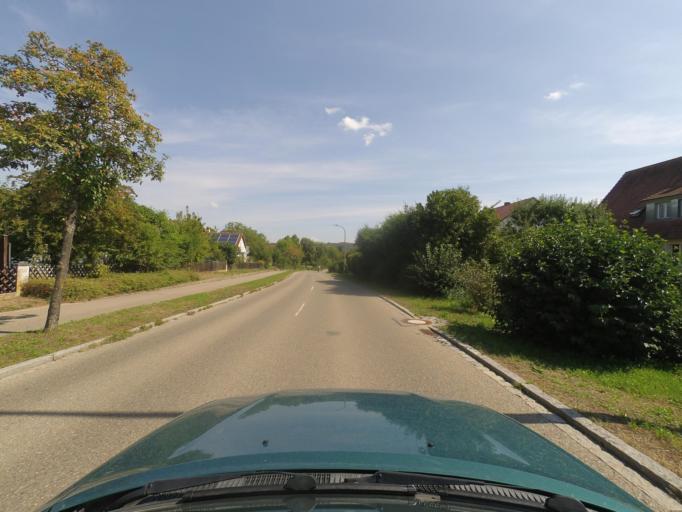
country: DE
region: Bavaria
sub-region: Regierungsbezirk Mittelfranken
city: Pleinfeld
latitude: 49.1031
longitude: 10.9782
